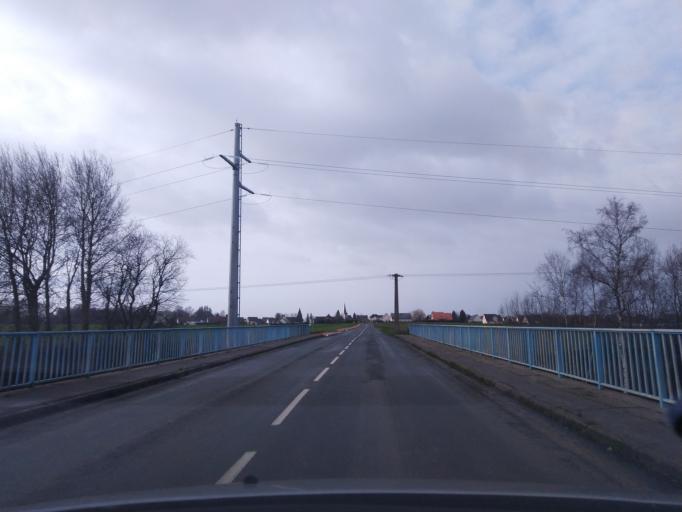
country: FR
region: Haute-Normandie
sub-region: Departement de la Seine-Maritime
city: Roumare
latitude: 49.5143
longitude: 0.9831
